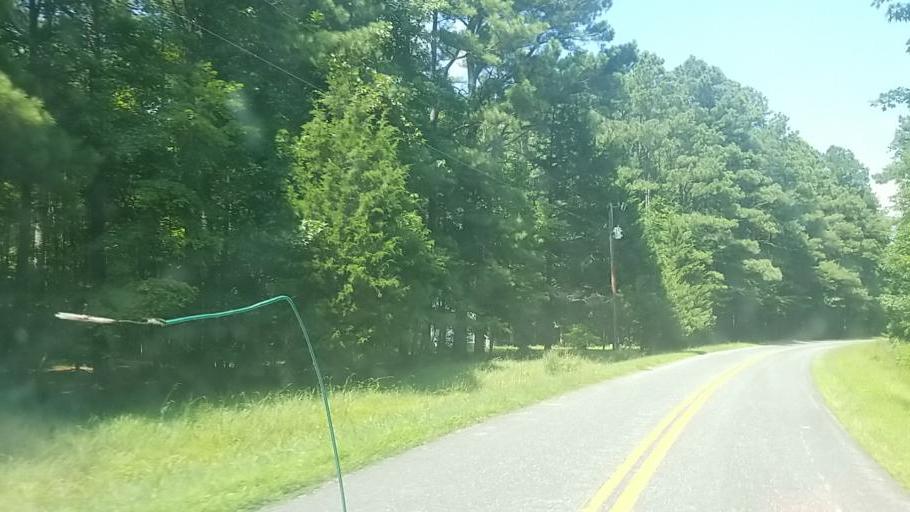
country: US
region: Maryland
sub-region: Wicomico County
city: Hebron
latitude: 38.4251
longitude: -75.8646
